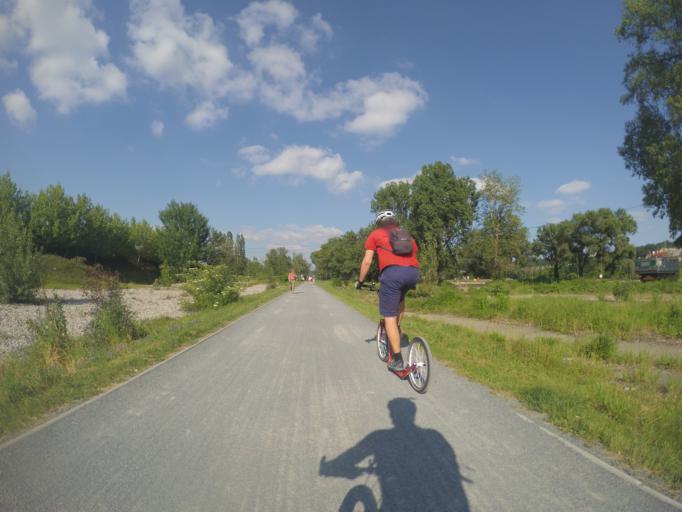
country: CZ
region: Praha
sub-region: Praha 8
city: Karlin
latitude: 50.0973
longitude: 14.4550
